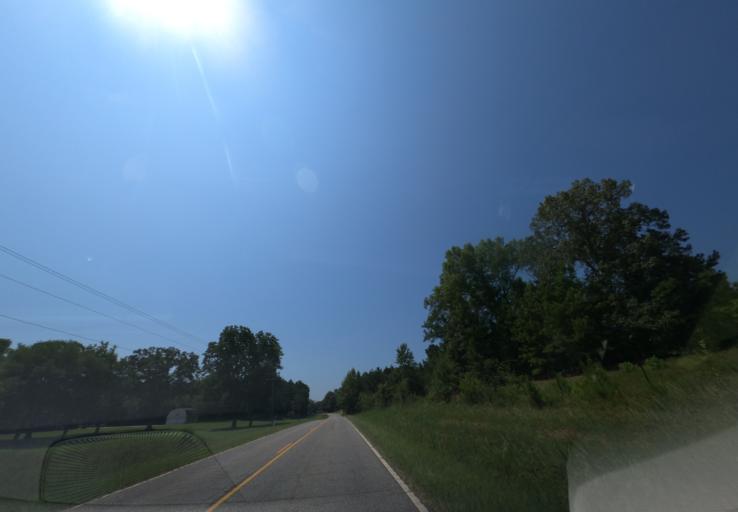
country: US
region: South Carolina
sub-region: Greenwood County
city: Greenwood
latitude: 34.0513
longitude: -82.1365
